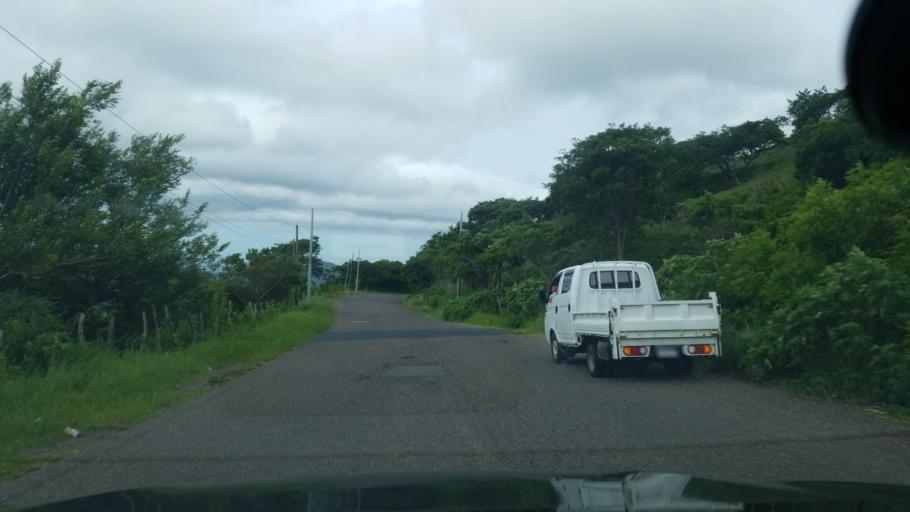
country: HN
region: Choluteca
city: Corpus
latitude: 13.3689
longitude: -86.9507
